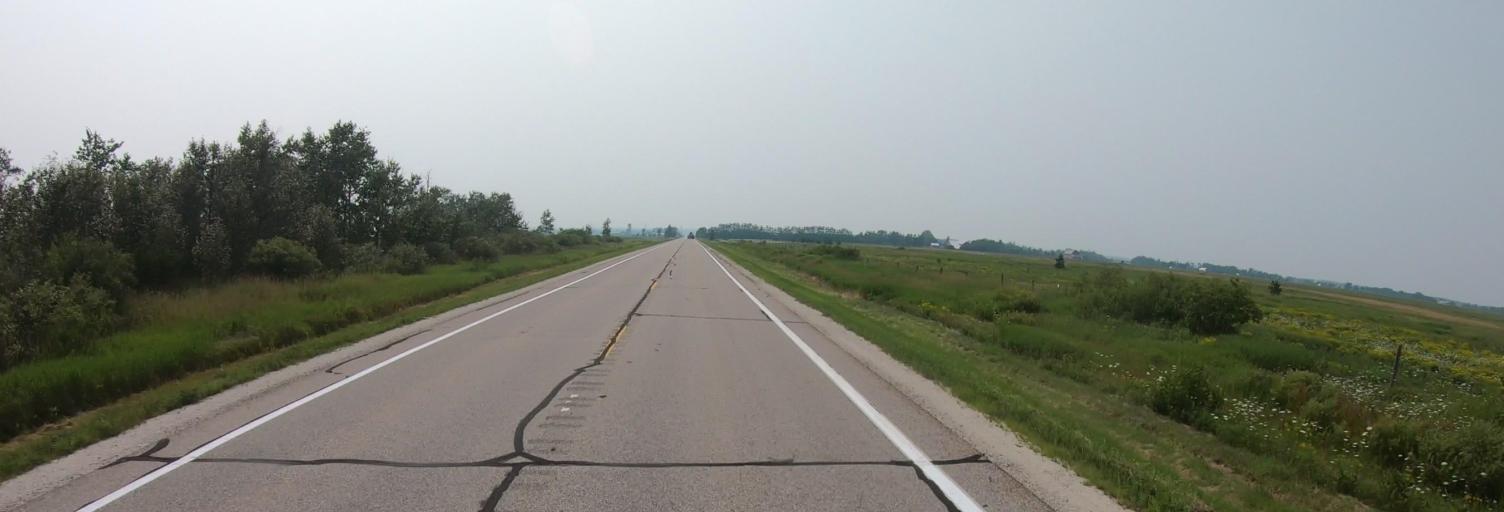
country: US
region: Michigan
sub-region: Chippewa County
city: Sault Ste. Marie
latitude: 46.1292
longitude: -84.3500
